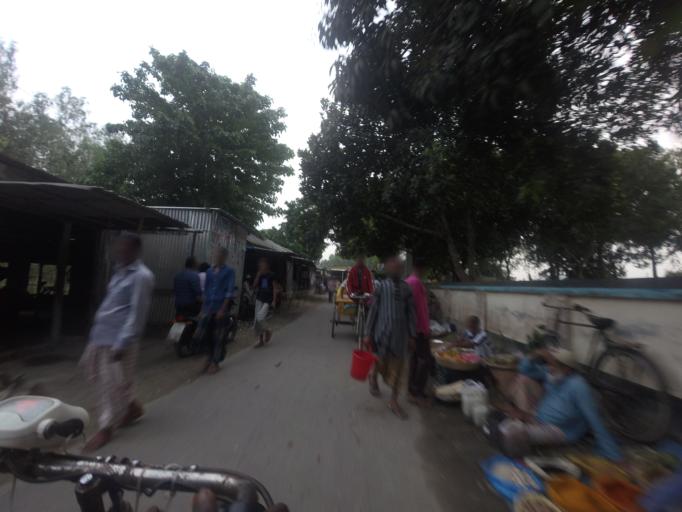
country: BD
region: Rajshahi
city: Sirajganj
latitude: 24.3151
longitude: 89.6718
